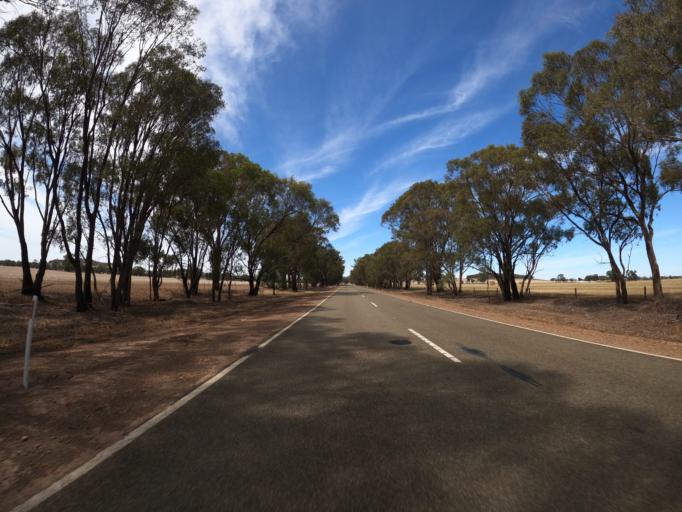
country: AU
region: Victoria
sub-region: Benalla
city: Benalla
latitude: -36.3126
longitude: 145.9583
